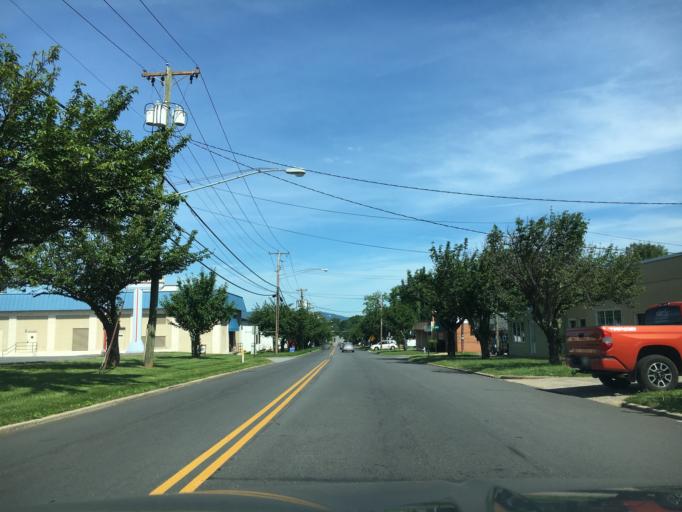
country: US
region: Virginia
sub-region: City of Lynchburg
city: West Lynchburg
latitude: 37.4010
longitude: -79.1743
